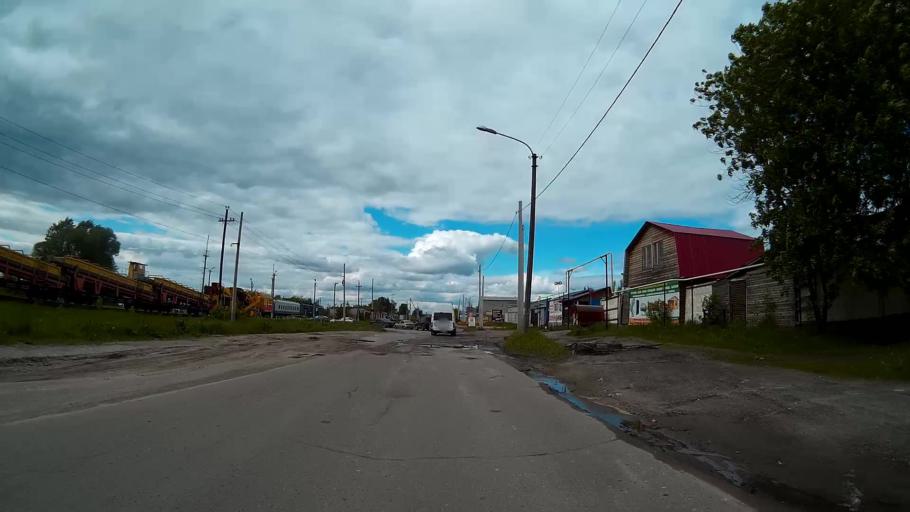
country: RU
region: Ulyanovsk
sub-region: Ulyanovskiy Rayon
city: Ulyanovsk
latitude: 54.2567
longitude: 48.3134
